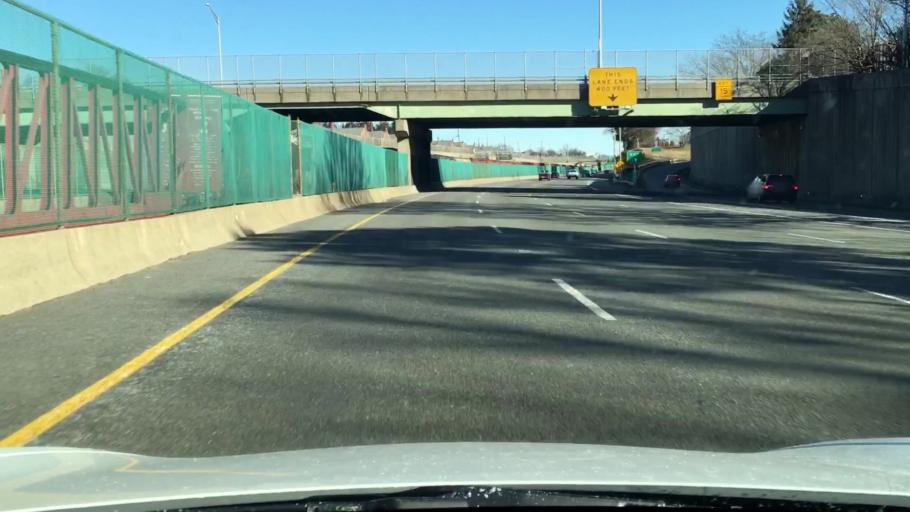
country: US
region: Virginia
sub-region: City of Richmond
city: Richmond
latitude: 37.5596
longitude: -77.4887
